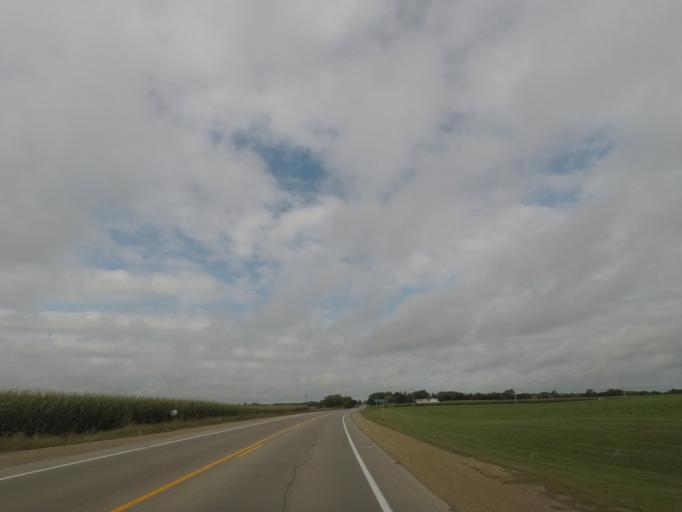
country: US
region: Wisconsin
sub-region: Dane County
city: Deerfield
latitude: 43.0335
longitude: -89.1281
